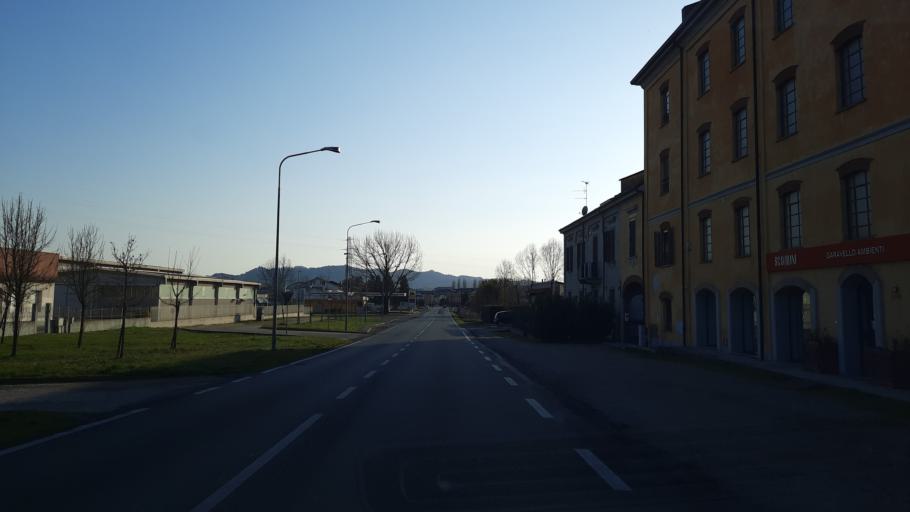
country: IT
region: Piedmont
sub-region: Provincia di Vercelli
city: Trino
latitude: 45.2060
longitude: 8.3019
